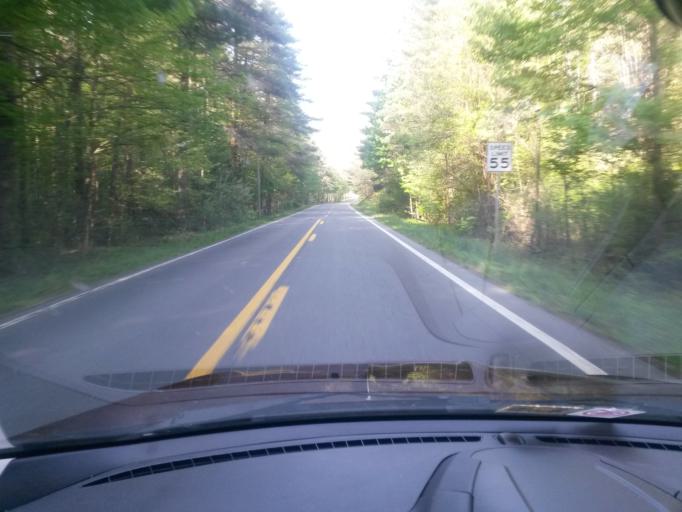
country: US
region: Virginia
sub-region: City of Covington
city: Covington
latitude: 37.9947
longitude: -80.0790
